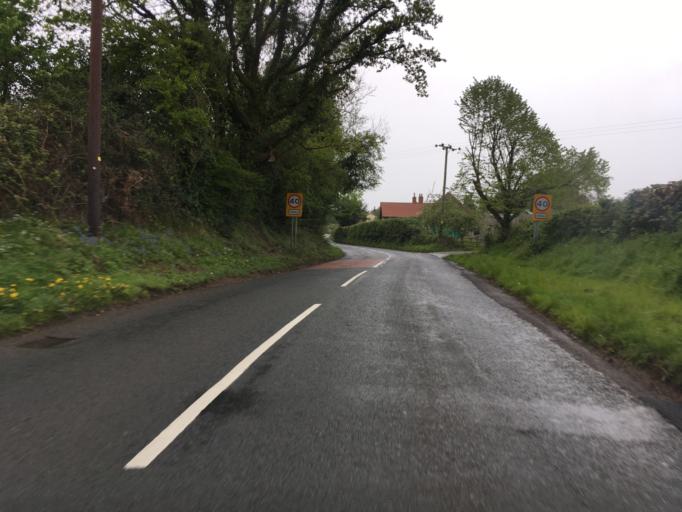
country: GB
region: England
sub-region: Bath and North East Somerset
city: Compton Martin
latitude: 51.3150
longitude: -2.6712
